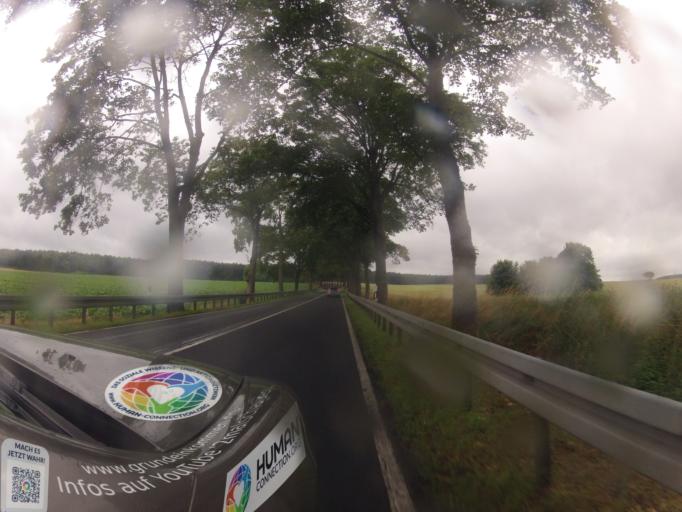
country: DE
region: Mecklenburg-Vorpommern
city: Seebad Bansin
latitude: 53.9027
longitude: 14.0470
